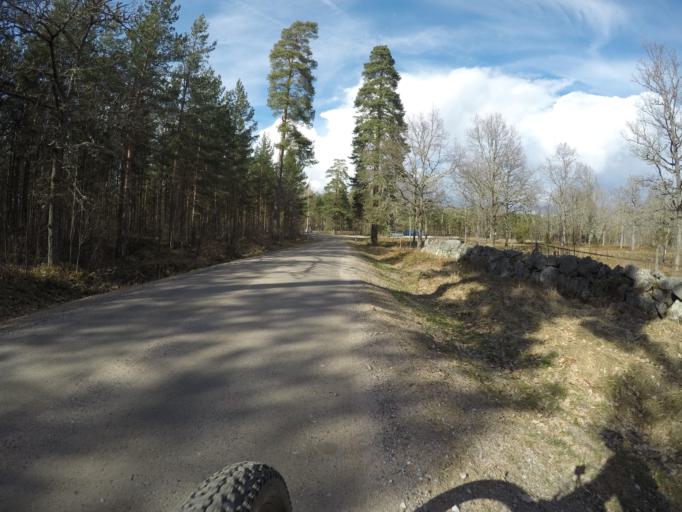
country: SE
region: Vaestmanland
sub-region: Kungsors Kommun
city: Kungsoer
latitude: 59.2786
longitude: 16.1222
